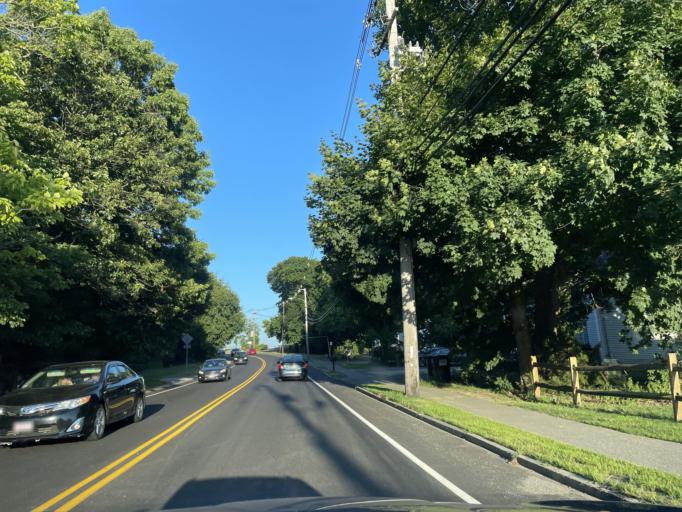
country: US
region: Massachusetts
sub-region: Plymouth County
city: Halifax
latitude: 41.9913
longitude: -70.8635
